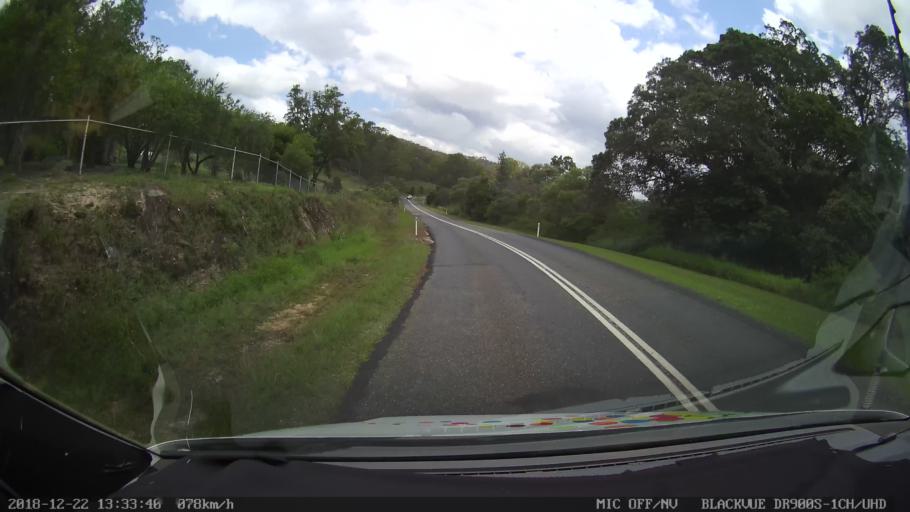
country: AU
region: New South Wales
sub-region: Clarence Valley
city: Coutts Crossing
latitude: -29.8640
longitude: 152.8247
